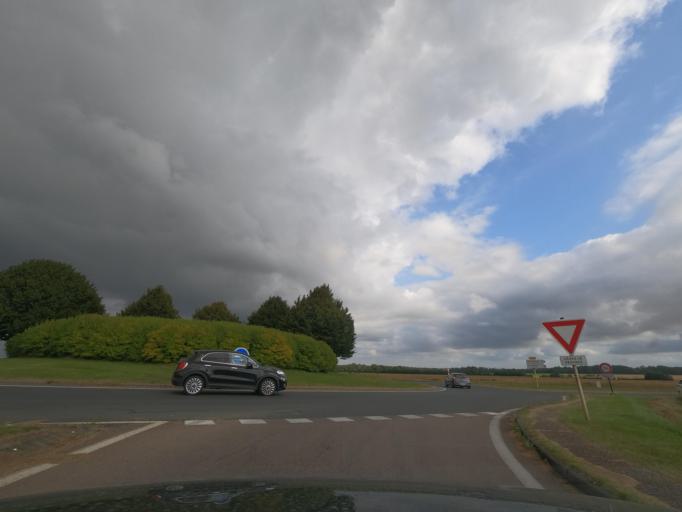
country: FR
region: Haute-Normandie
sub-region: Departement de l'Eure
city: Menneval
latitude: 49.1149
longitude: 0.6213
